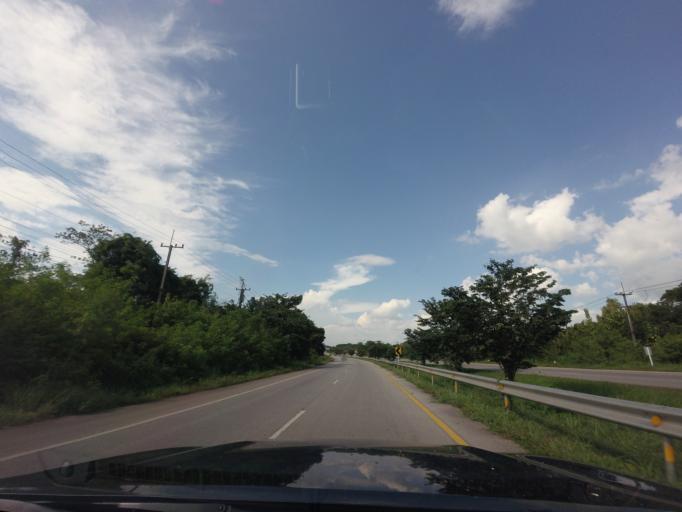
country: TH
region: Nong Khai
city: Sa Khrai
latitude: 17.6580
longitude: 102.7904
